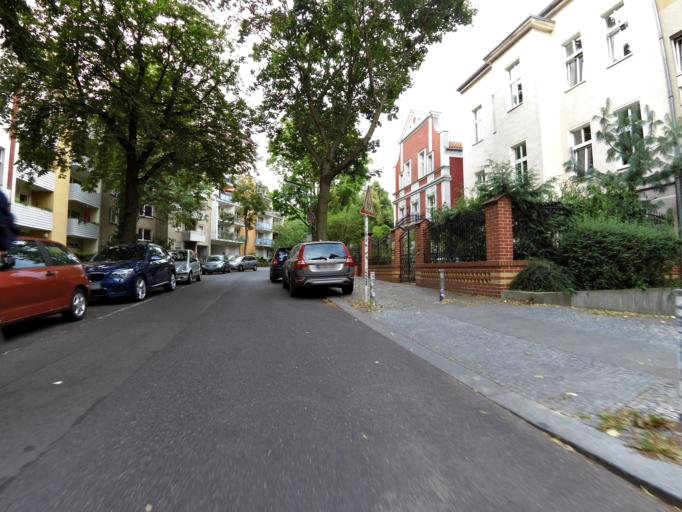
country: DE
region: Berlin
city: Friedenau
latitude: 52.4688
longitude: 13.3372
